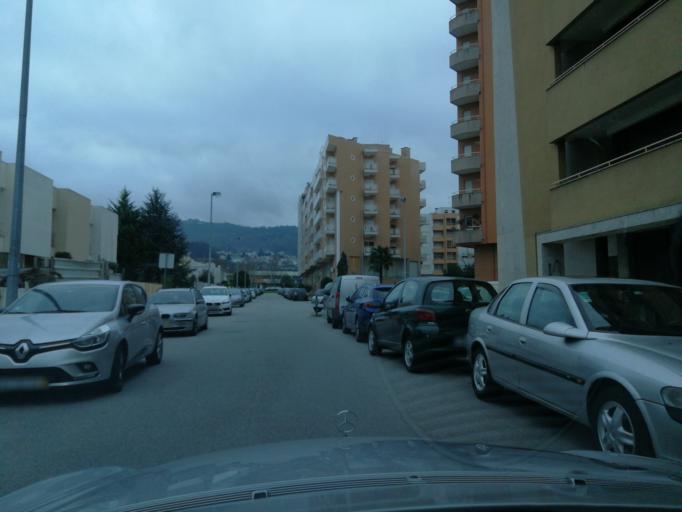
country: PT
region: Braga
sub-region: Braga
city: Braga
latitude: 41.5510
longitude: -8.4040
